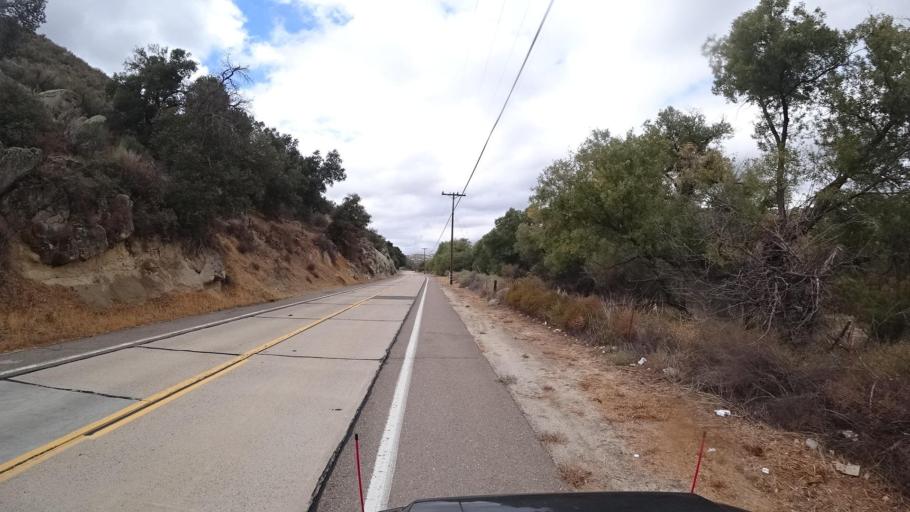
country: US
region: California
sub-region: San Diego County
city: Campo
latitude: 32.7235
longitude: -116.4348
